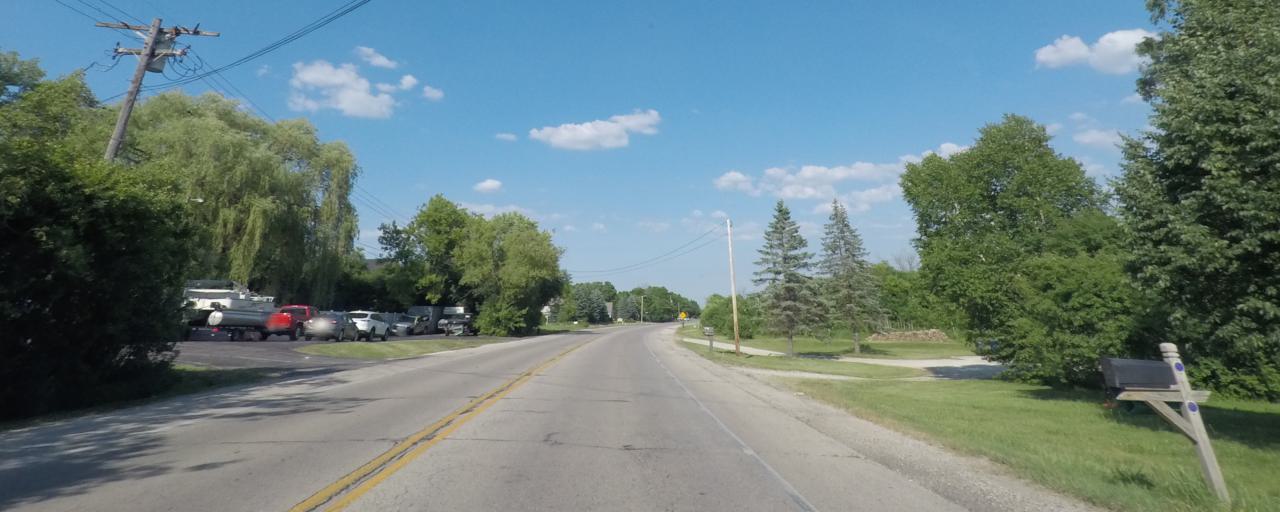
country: US
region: Wisconsin
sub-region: Waukesha County
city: Big Bend
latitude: 42.8924
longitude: -88.1734
